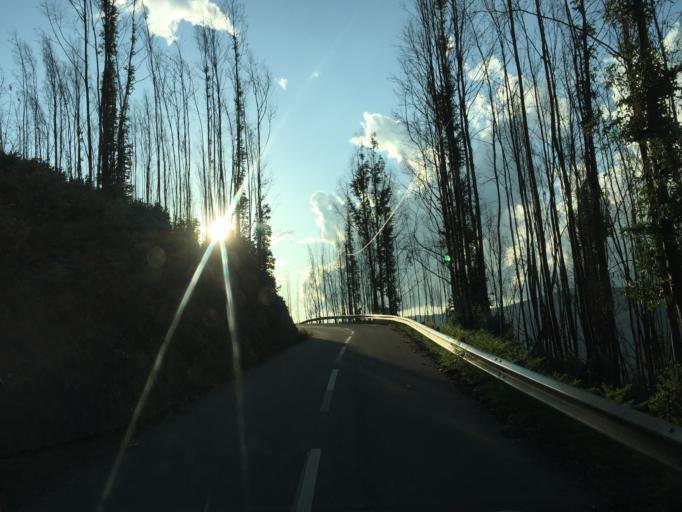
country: PT
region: Coimbra
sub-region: Arganil
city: Arganil
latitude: 40.1315
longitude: -8.0057
